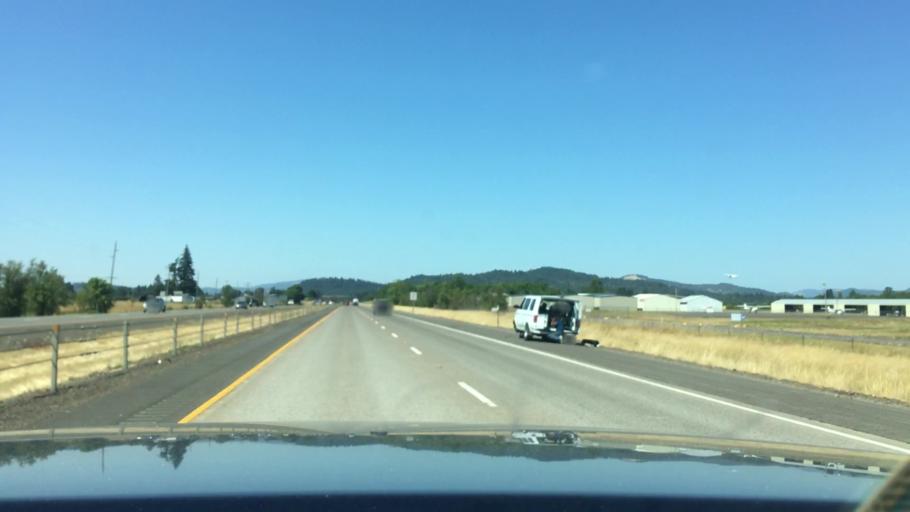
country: US
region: Oregon
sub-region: Lane County
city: Creswell
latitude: 43.9291
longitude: -123.0107
